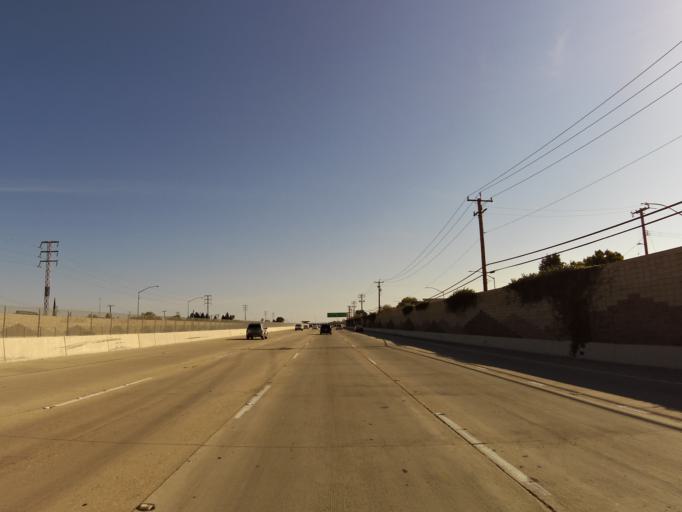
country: US
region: California
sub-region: Contra Costa County
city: Pittsburg
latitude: 38.0189
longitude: -121.8974
